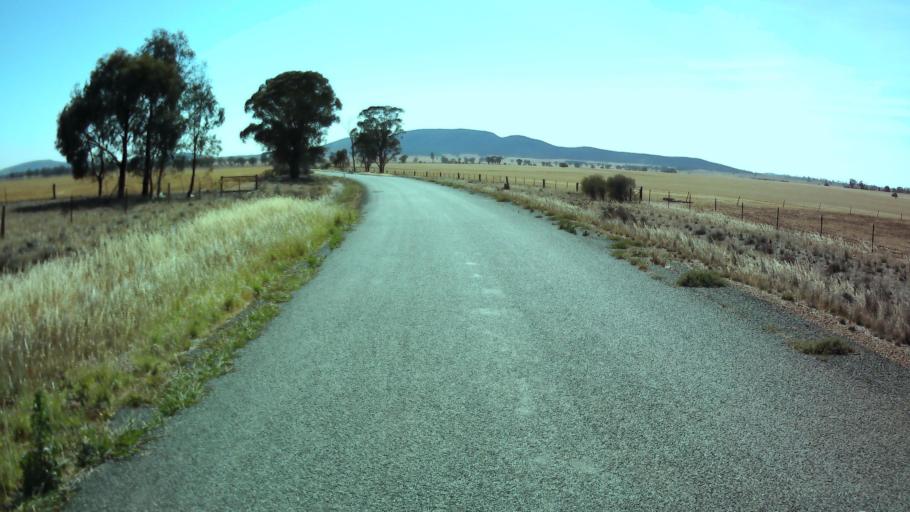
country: AU
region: New South Wales
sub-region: Weddin
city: Grenfell
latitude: -33.7529
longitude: 147.8646
